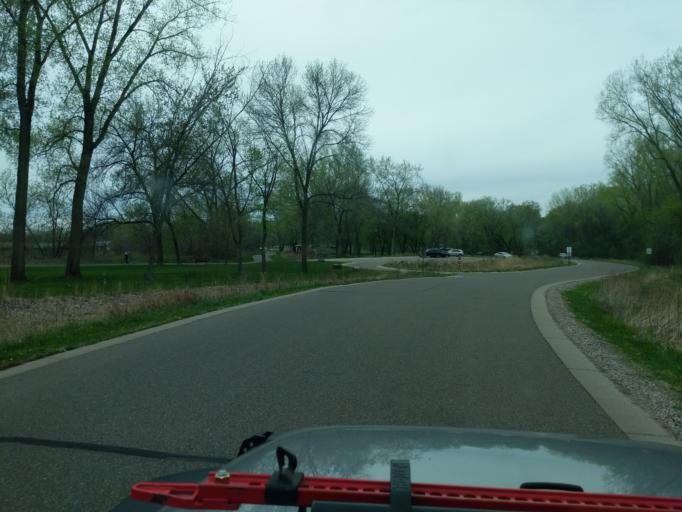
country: US
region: Minnesota
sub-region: Anoka County
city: Coon Rapids
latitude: 45.1452
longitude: -93.3041
